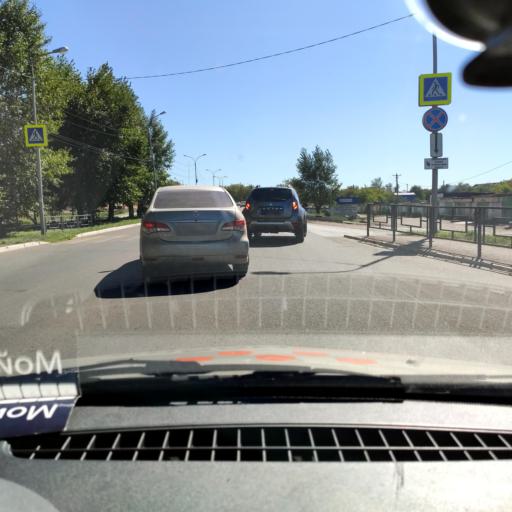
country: RU
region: Bashkortostan
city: Kumertau
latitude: 52.7602
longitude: 55.8093
